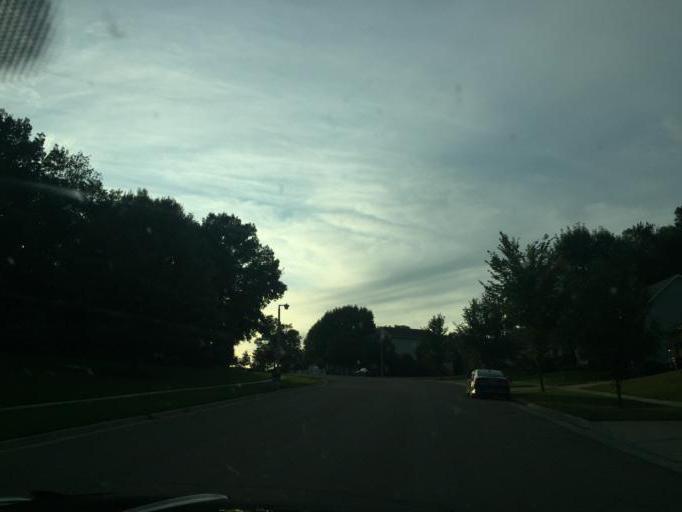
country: US
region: Minnesota
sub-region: Olmsted County
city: Rochester
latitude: 44.0105
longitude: -92.4965
